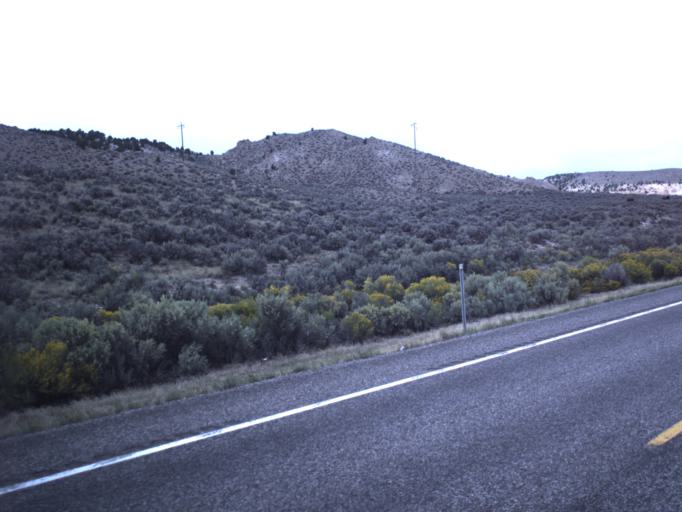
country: US
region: Utah
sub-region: Garfield County
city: Panguitch
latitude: 38.0132
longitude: -112.3726
